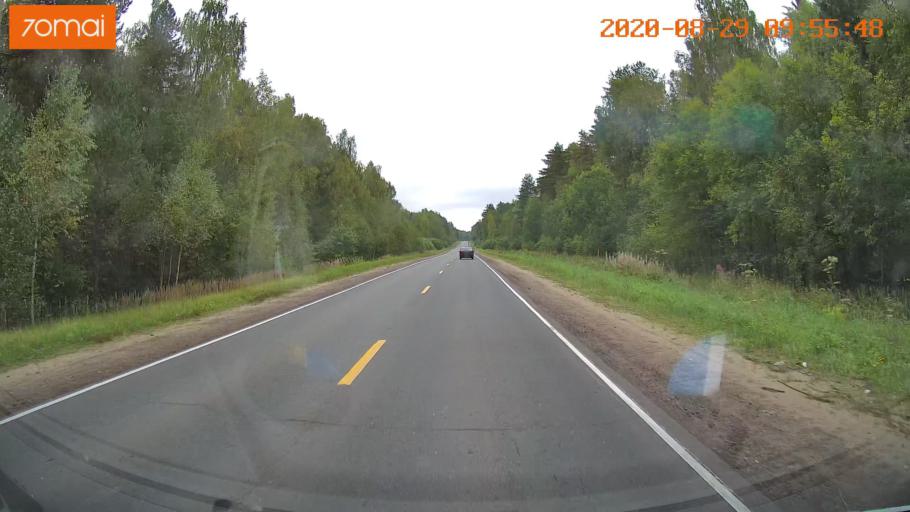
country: RU
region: Ivanovo
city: Zarechnyy
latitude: 57.4217
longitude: 42.2726
